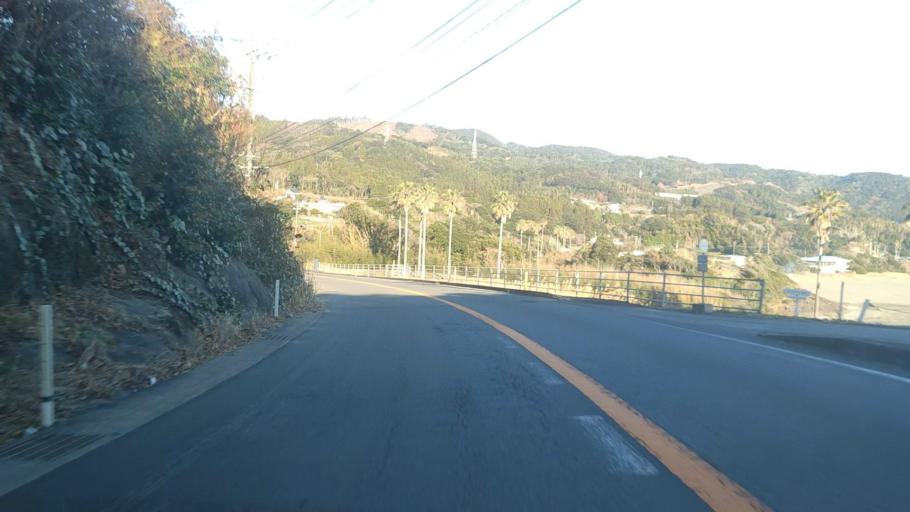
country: JP
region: Miyazaki
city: Nobeoka
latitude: 32.3526
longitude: 131.6230
